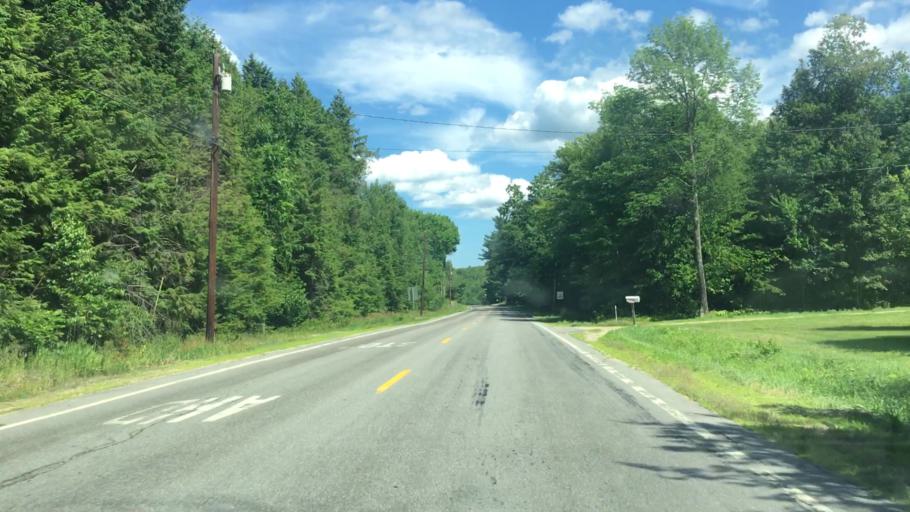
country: US
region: Maine
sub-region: Franklin County
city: Wilton
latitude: 44.5769
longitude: -70.1720
